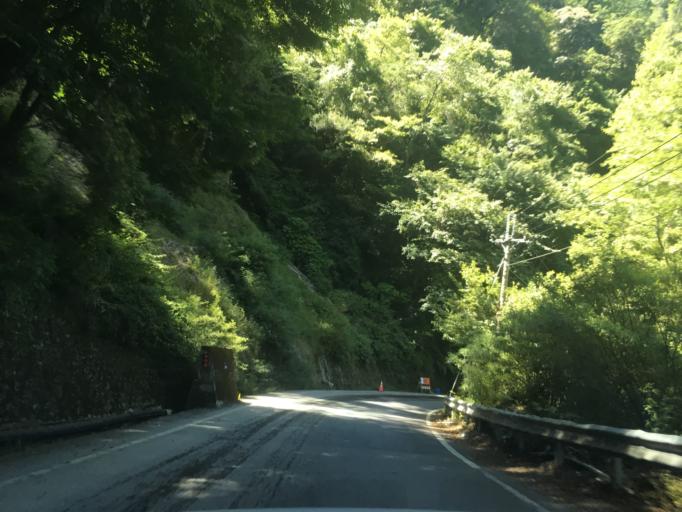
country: TW
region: Taiwan
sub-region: Nantou
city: Puli
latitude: 24.2133
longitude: 121.2675
